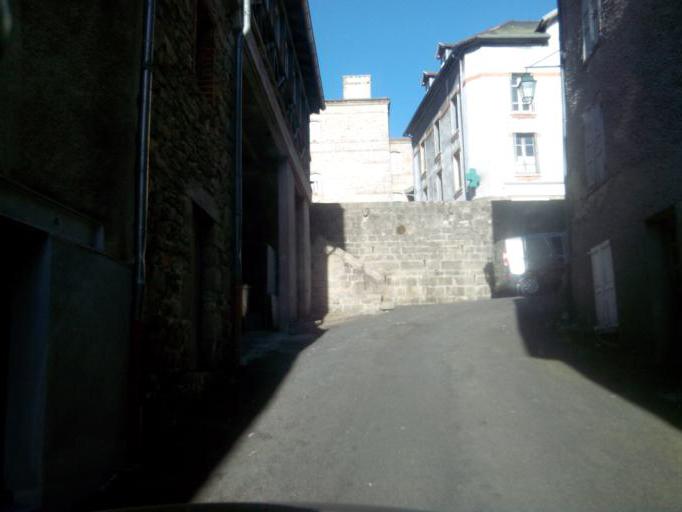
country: FR
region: Auvergne
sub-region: Departement de la Haute-Loire
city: Fontannes
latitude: 45.3204
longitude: 3.6953
